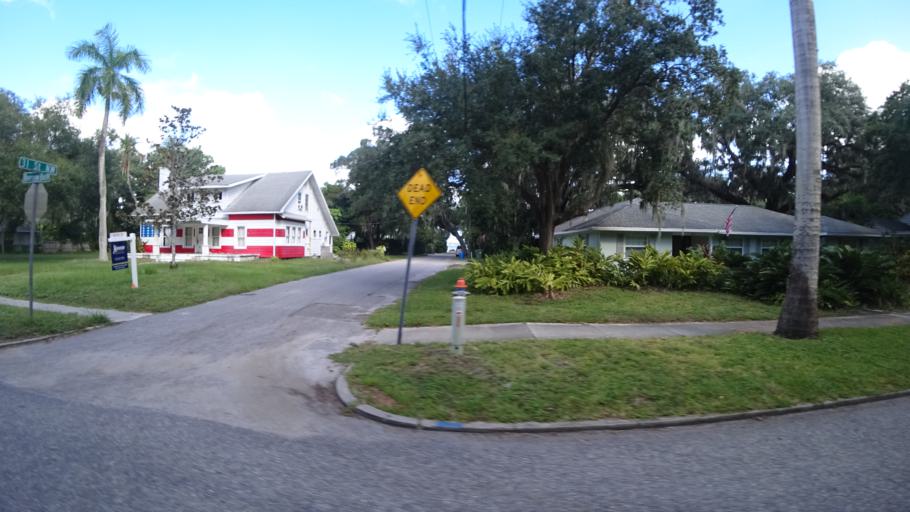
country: US
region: Florida
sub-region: Manatee County
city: Bradenton
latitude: 27.5011
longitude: -82.5926
